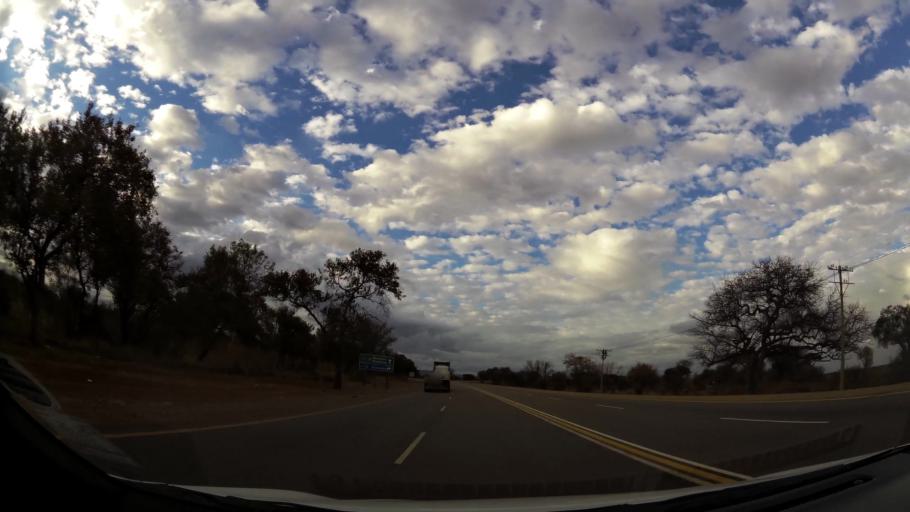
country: ZA
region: Limpopo
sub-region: Waterberg District Municipality
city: Modimolle
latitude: -24.5045
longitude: 28.7294
